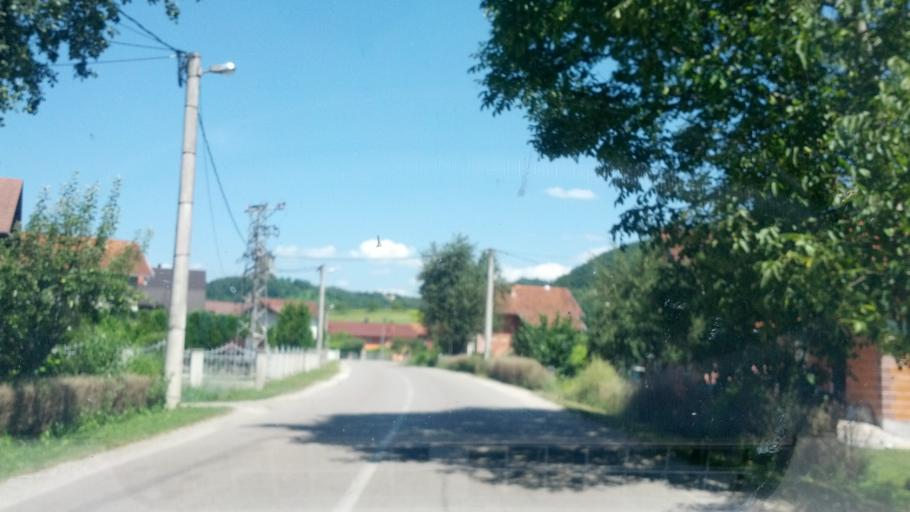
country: BA
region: Federation of Bosnia and Herzegovina
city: Otoka
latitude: 44.9708
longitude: 16.1796
